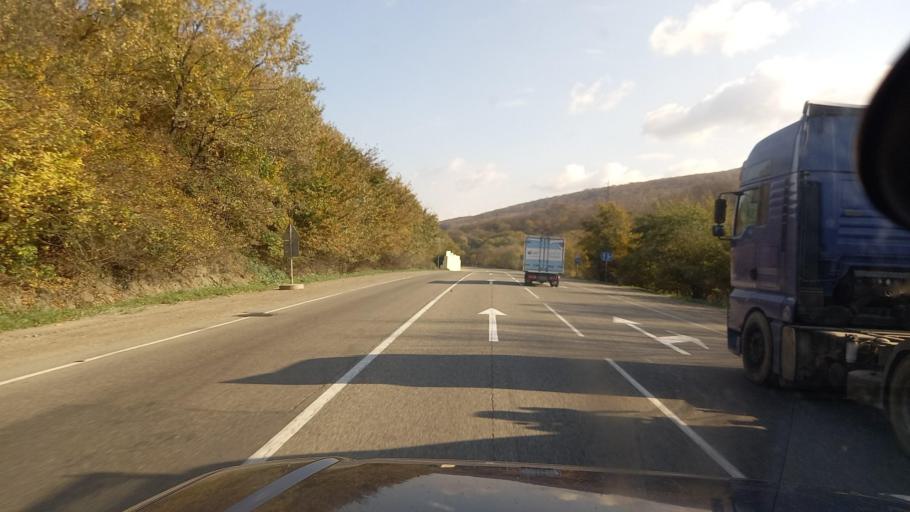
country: RU
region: Krasnodarskiy
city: Verkhnebakanskiy
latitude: 44.8428
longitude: 37.7141
